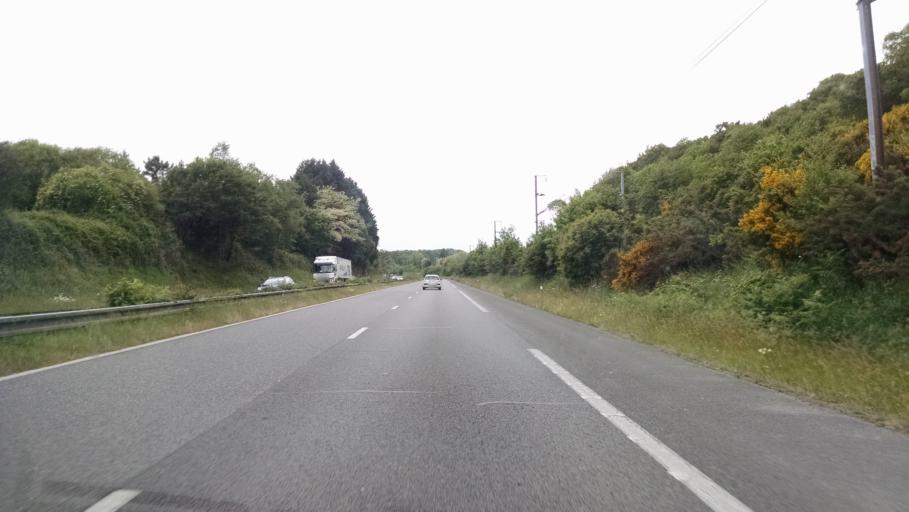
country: FR
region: Brittany
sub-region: Departement du Finistere
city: Quimperle
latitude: 47.8556
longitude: -3.5235
